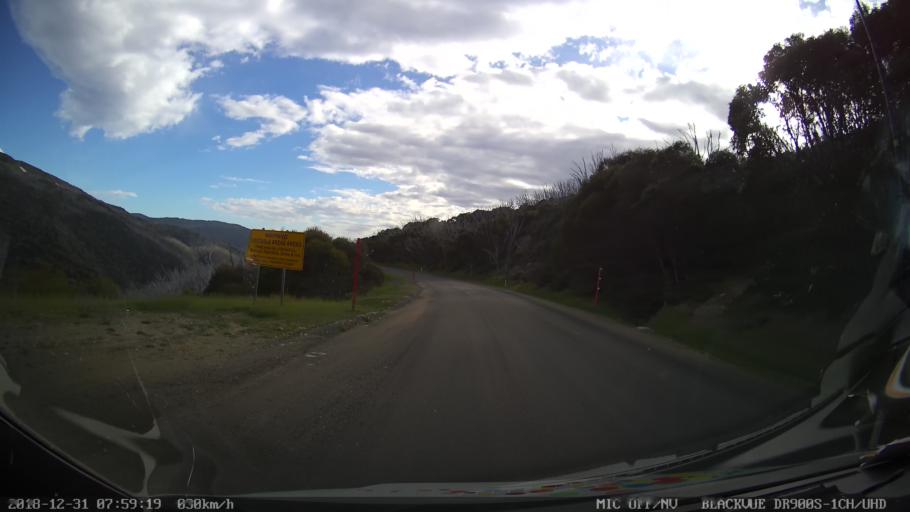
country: AU
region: New South Wales
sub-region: Snowy River
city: Jindabyne
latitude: -36.3718
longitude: 148.3847
